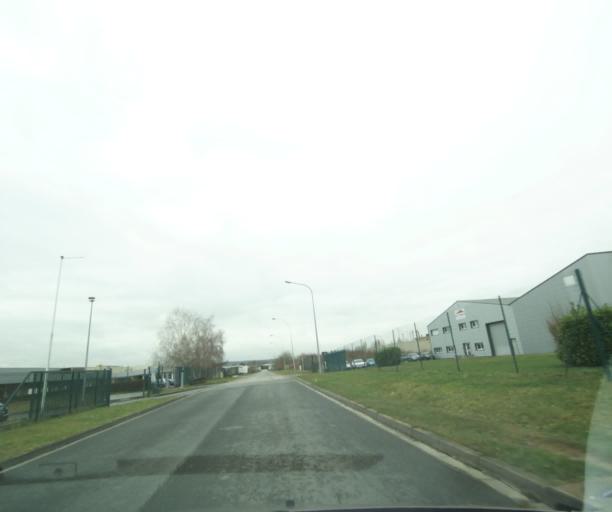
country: FR
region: Picardie
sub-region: Departement de l'Oise
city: Noyon
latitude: 49.5731
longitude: 3.0277
